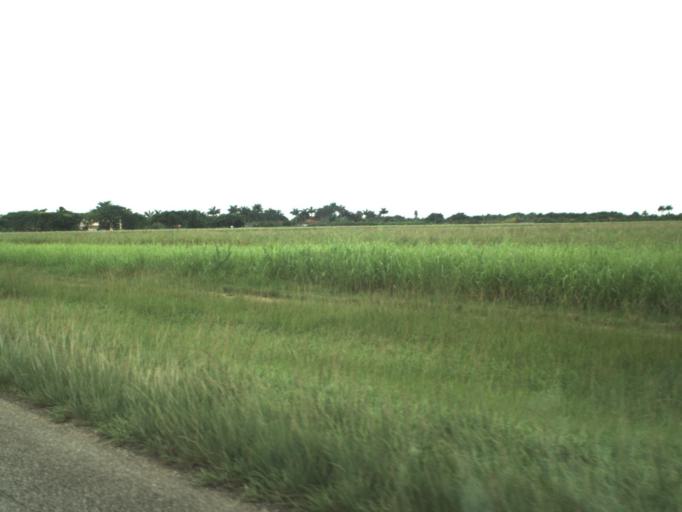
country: US
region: Florida
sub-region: Miami-Dade County
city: Country Walk
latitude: 25.6347
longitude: -80.4798
